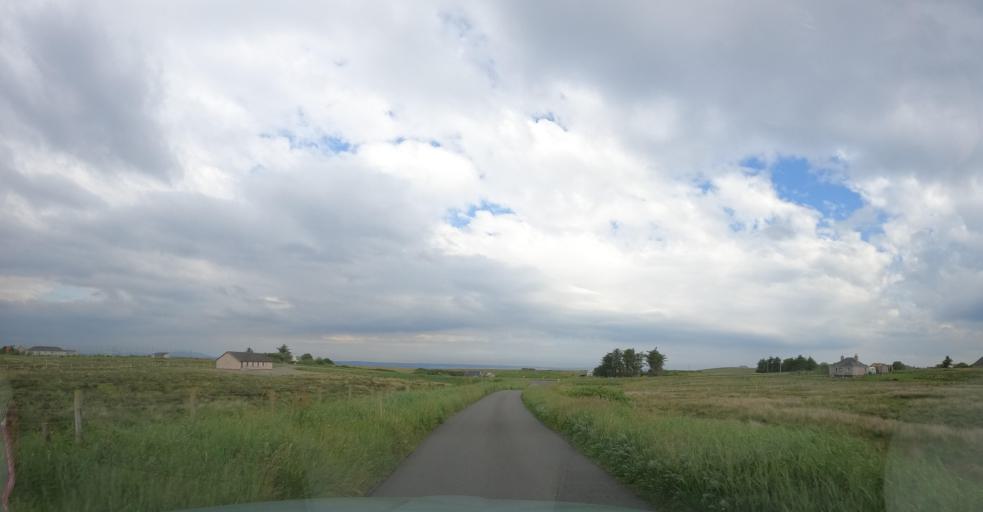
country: GB
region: Scotland
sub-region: Eilean Siar
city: Stornoway
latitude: 58.2082
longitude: -6.2506
